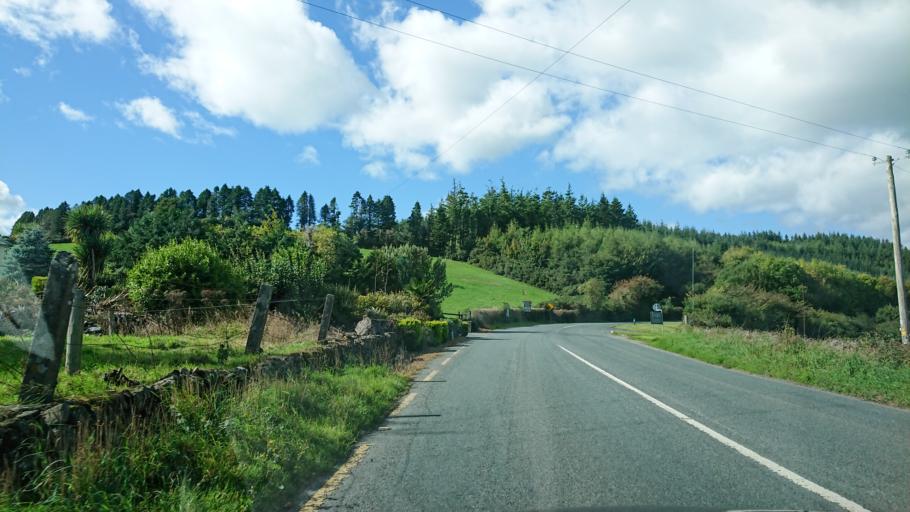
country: IE
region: Munster
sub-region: Waterford
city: Dungarvan
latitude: 52.1183
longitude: -7.6854
